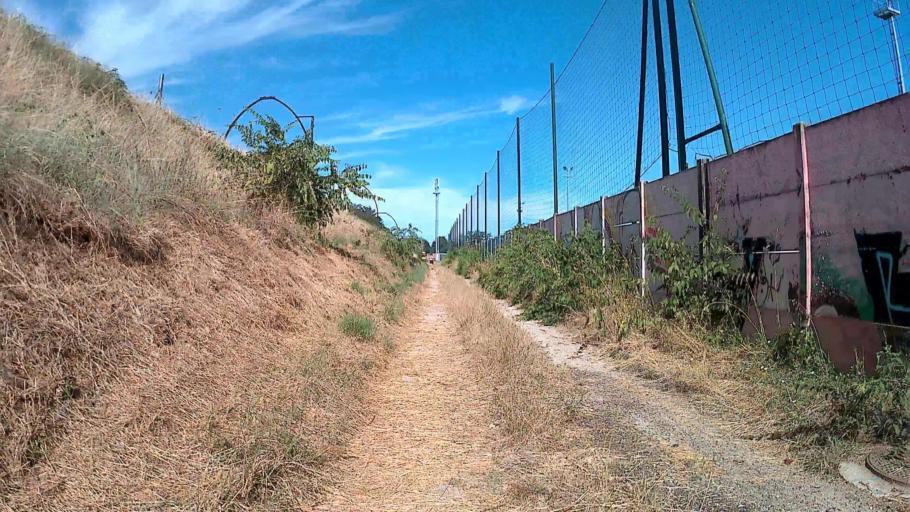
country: FR
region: Aquitaine
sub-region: Departement de la Gironde
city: Bruges
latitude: 44.8722
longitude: -0.6054
